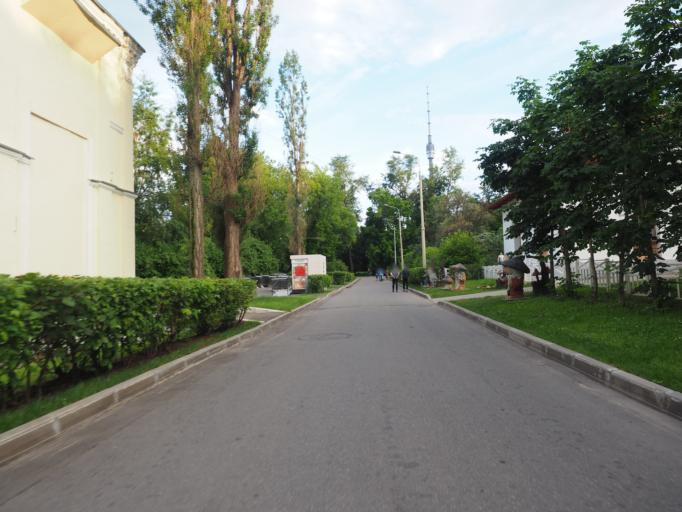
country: RU
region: Moscow
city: Ostankinskiy
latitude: 55.8316
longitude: 37.6168
